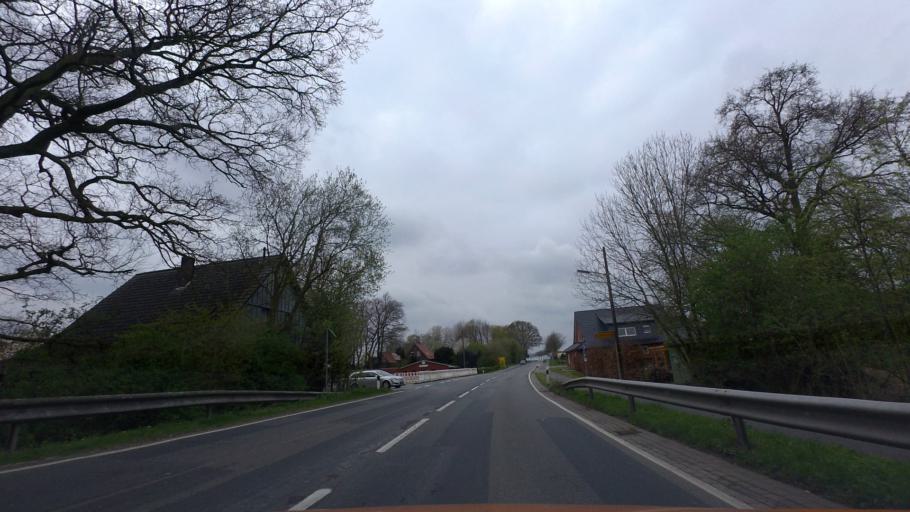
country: DE
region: Lower Saxony
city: Wildeshausen
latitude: 52.8802
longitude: 8.4003
